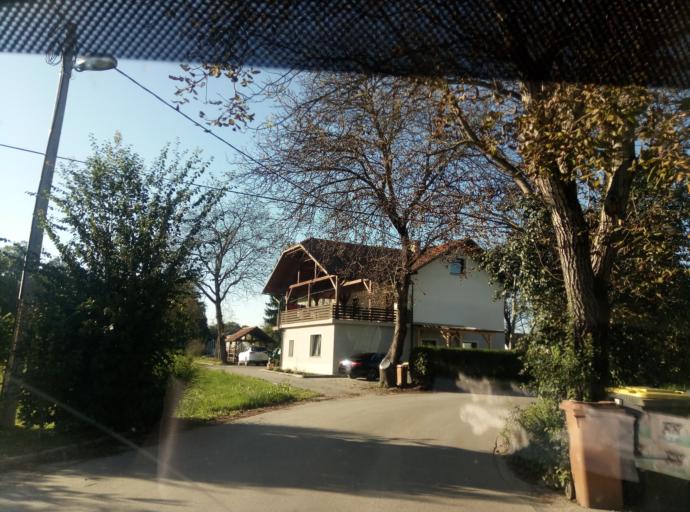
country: SI
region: Ljubljana
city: Ljubljana
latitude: 46.0975
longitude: 14.5031
